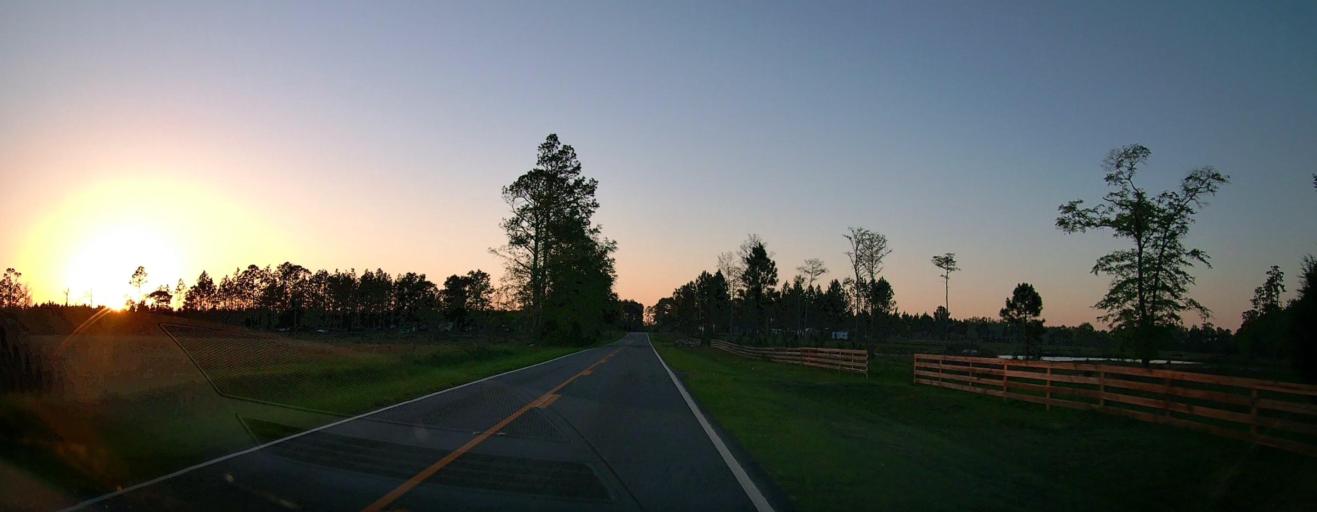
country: US
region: Georgia
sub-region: Wilcox County
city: Rochelle
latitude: 31.8052
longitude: -83.4569
